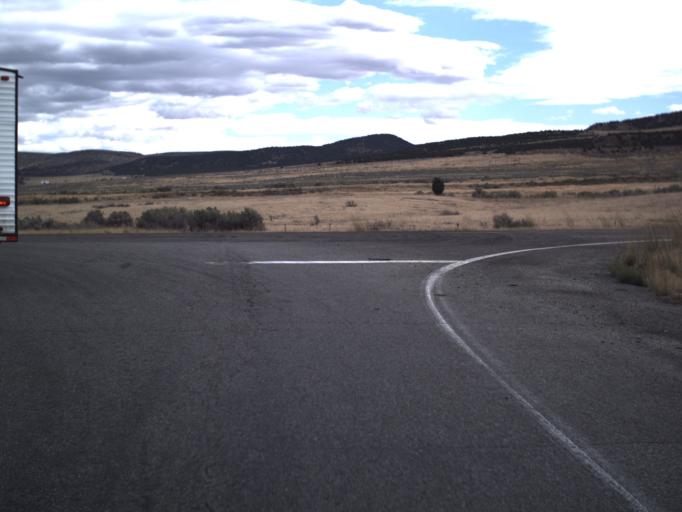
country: US
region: Idaho
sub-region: Oneida County
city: Malad City
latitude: 41.9599
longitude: -112.7105
